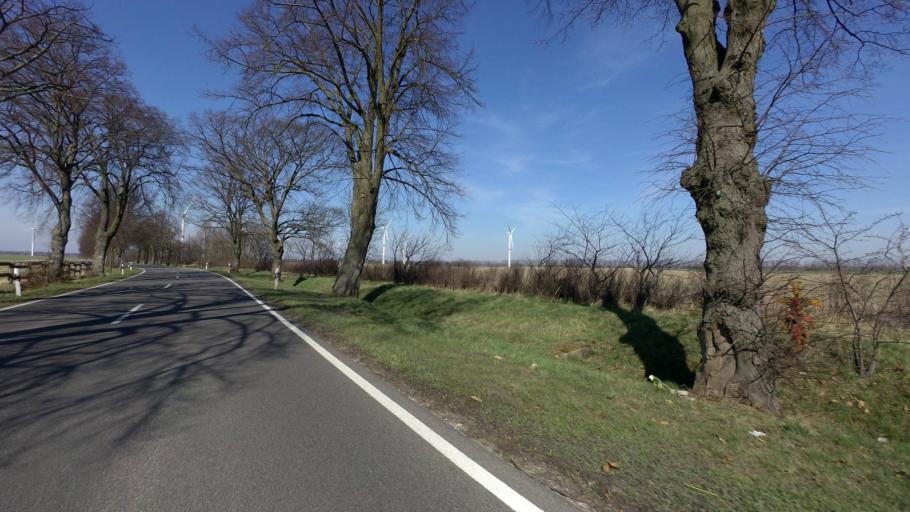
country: DE
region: Brandenburg
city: Eberswalde
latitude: 52.7462
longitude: 13.8446
